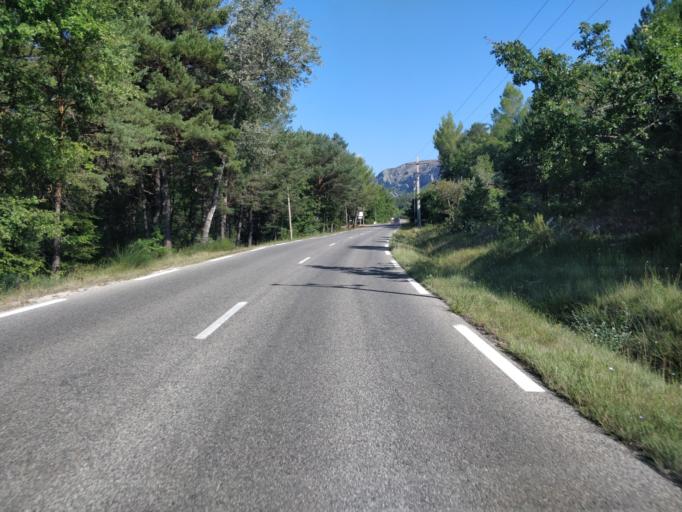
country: FR
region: Provence-Alpes-Cote d'Azur
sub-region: Departement des Alpes-de-Haute-Provence
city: Riez
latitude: 43.8134
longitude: 6.2264
